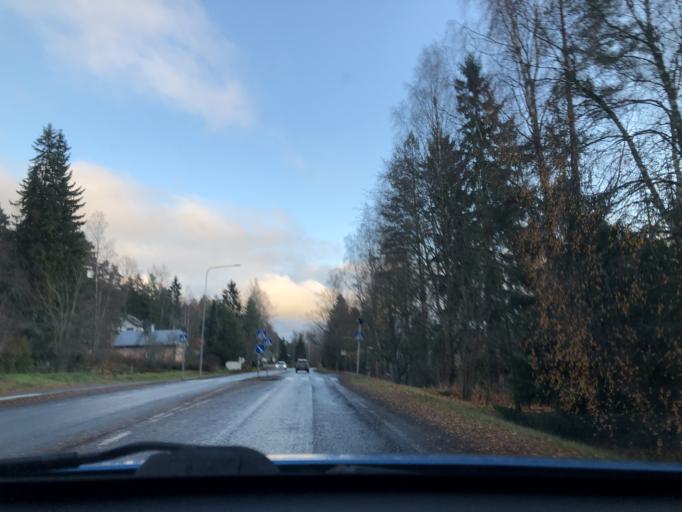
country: FI
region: Pirkanmaa
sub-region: Tampere
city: Kangasala
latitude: 61.4678
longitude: 24.0481
